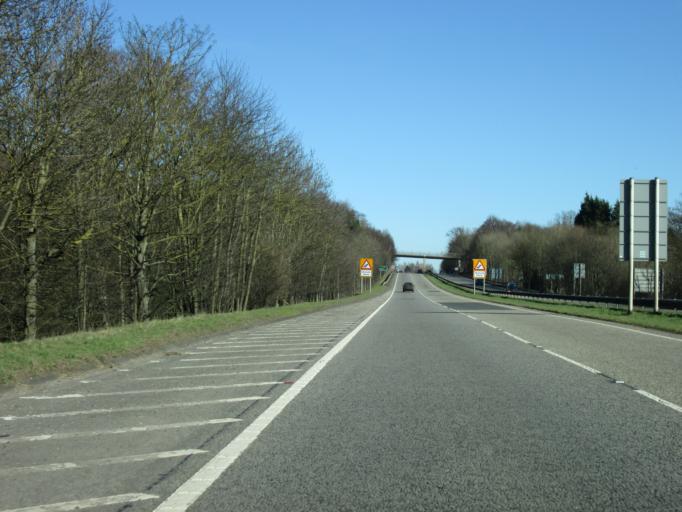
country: GB
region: England
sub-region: Northumberland
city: Acomb
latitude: 54.9839
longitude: -2.1079
